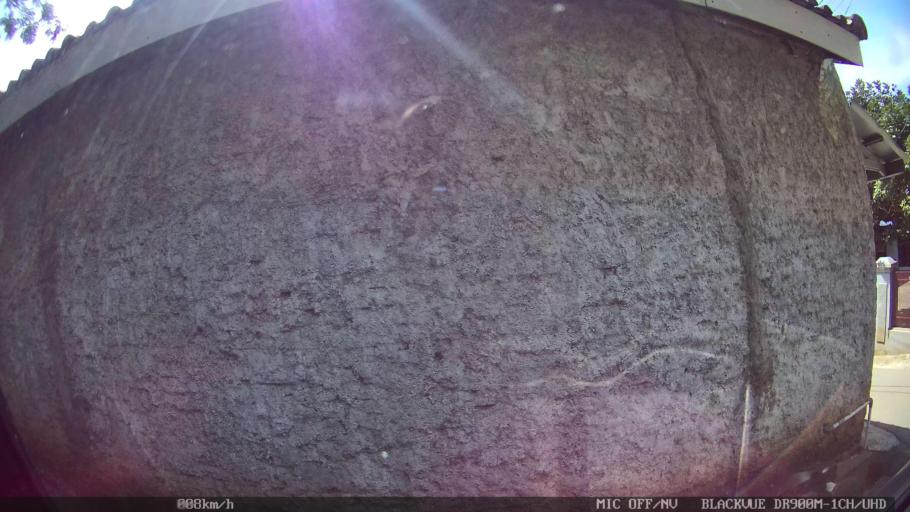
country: ID
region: Lampung
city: Kedaton
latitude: -5.3671
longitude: 105.2498
